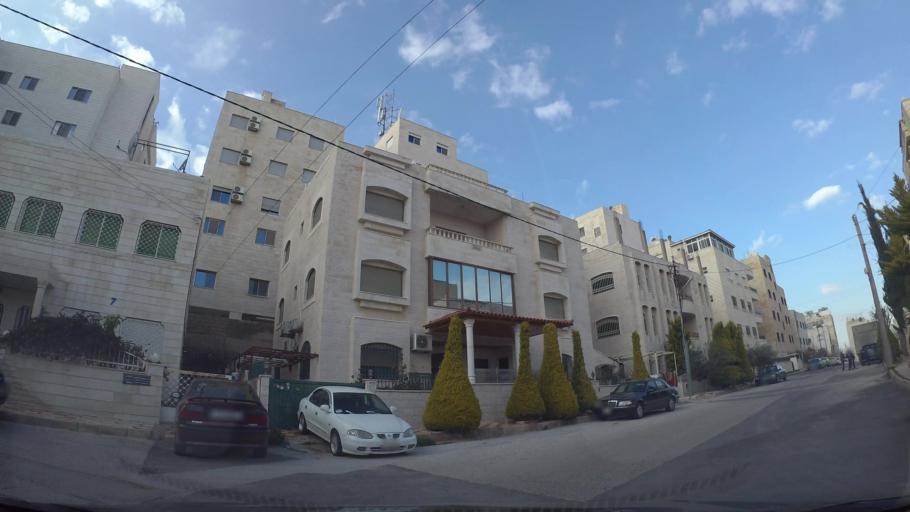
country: JO
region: Amman
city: Al Bunayyat ash Shamaliyah
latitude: 31.9144
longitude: 35.8883
